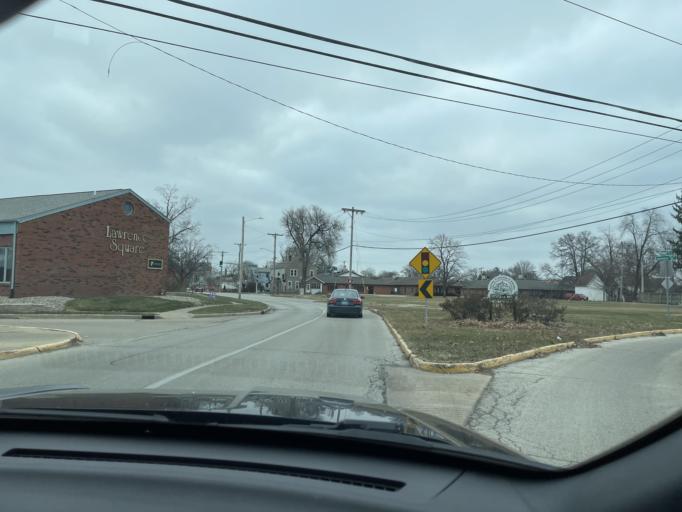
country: US
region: Illinois
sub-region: Sangamon County
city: Springfield
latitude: 39.7942
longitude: -89.6588
